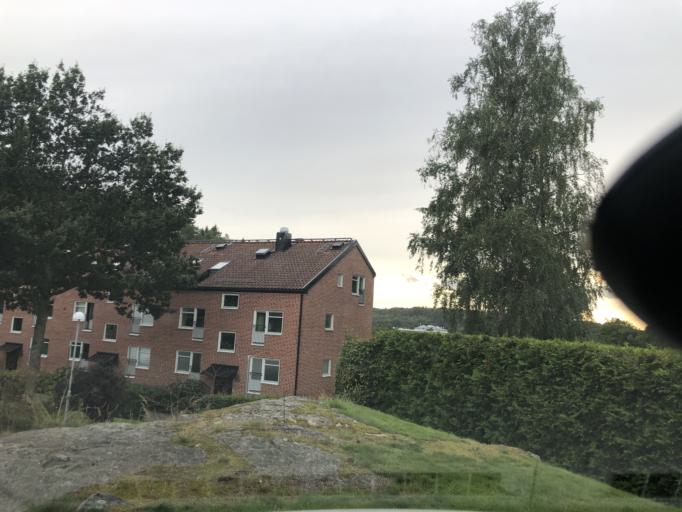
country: SE
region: Vaestra Goetaland
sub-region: Goteborg
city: Goeteborg
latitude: 57.7477
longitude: 11.9593
